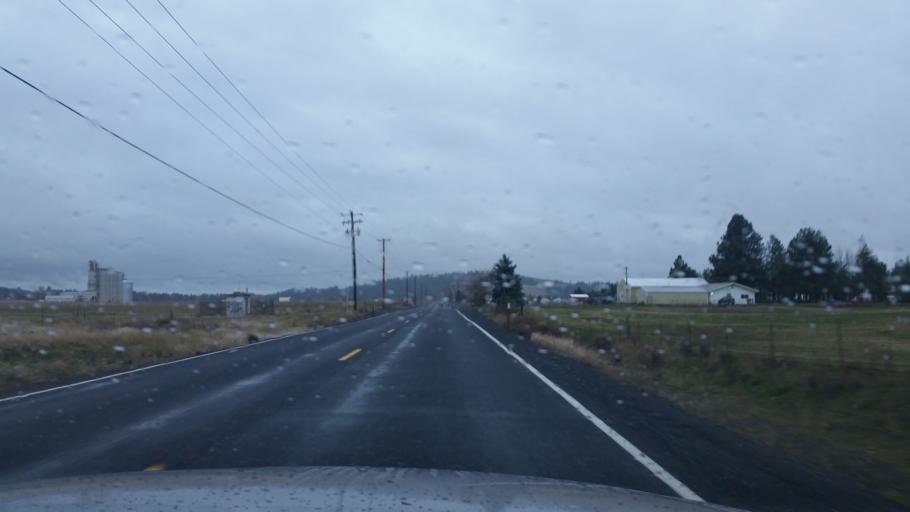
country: US
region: Washington
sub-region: Spokane County
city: Fairchild Air Force Base
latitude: 47.5812
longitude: -117.6076
